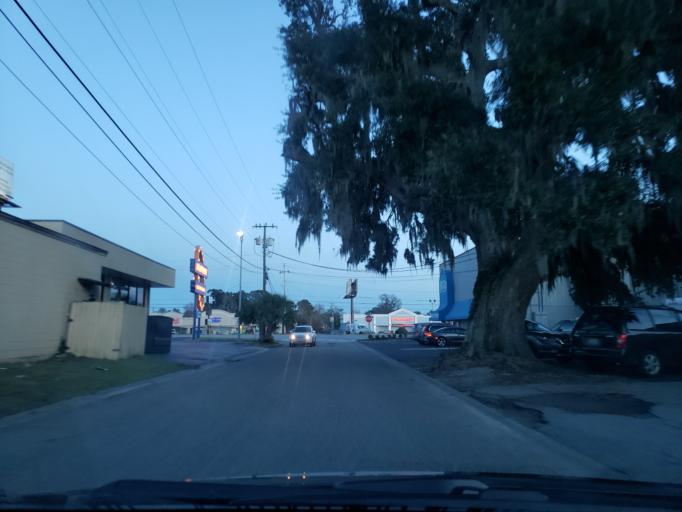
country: US
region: Georgia
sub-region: Chatham County
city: Isle of Hope
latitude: 32.0082
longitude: -81.1162
